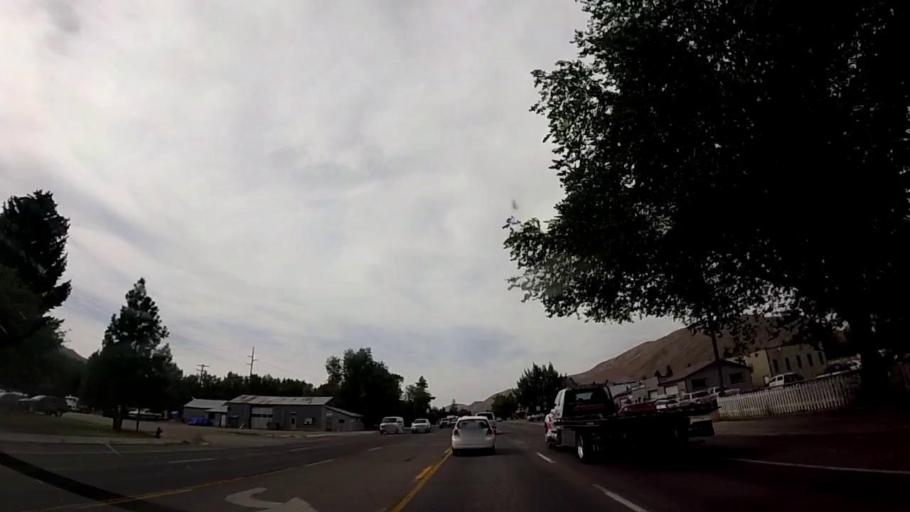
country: US
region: Idaho
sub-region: Blaine County
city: Bellevue
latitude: 43.4605
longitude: -114.2591
